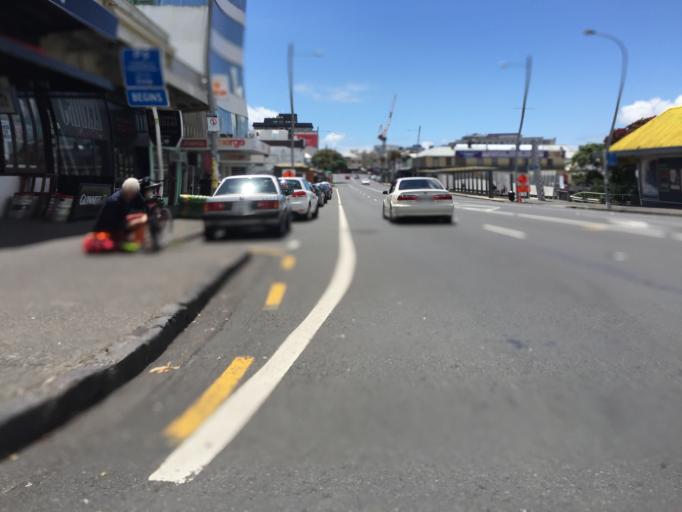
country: NZ
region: Auckland
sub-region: Auckland
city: Auckland
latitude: -36.8586
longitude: 174.7550
